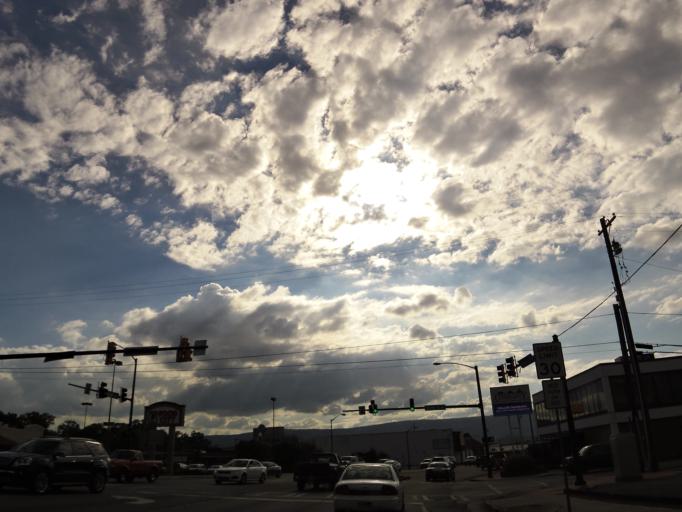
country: US
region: Georgia
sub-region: Walker County
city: Rossville
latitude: 34.9830
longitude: -85.2841
